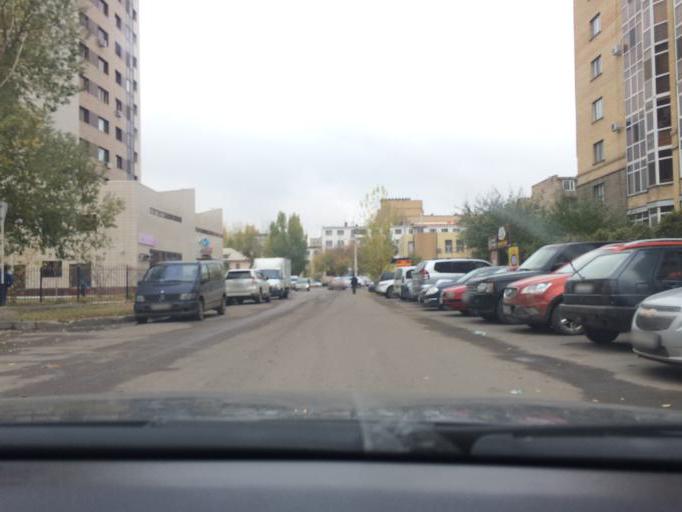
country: KZ
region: Astana Qalasy
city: Astana
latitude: 51.1656
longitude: 71.4378
